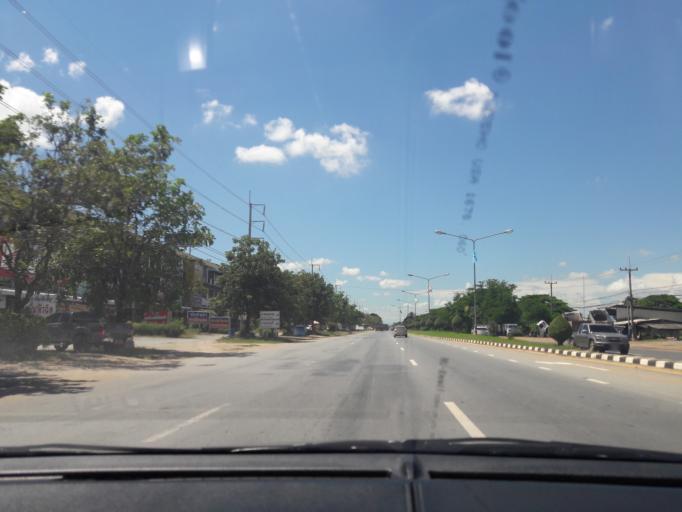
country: TH
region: Kanchanaburi
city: Tha Maka
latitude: 14.0412
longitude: 99.7881
